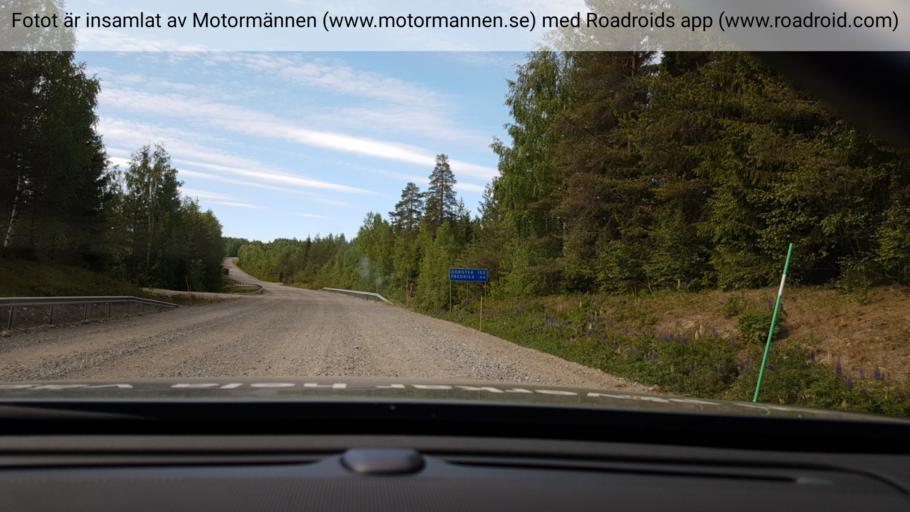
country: SE
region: Vaesterbotten
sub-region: Bjurholms Kommun
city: Bjurholm
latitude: 63.9272
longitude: 19.1886
